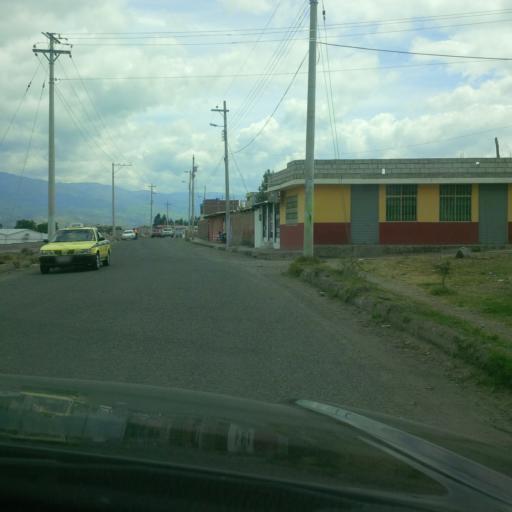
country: EC
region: Chimborazo
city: Riobamba
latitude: -1.6529
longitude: -78.6493
